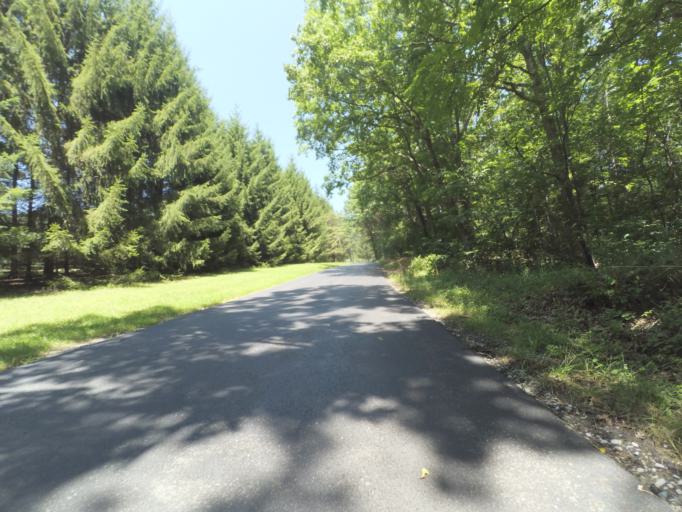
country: US
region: Pennsylvania
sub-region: Centre County
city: Boalsburg
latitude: 40.8078
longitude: -77.7689
